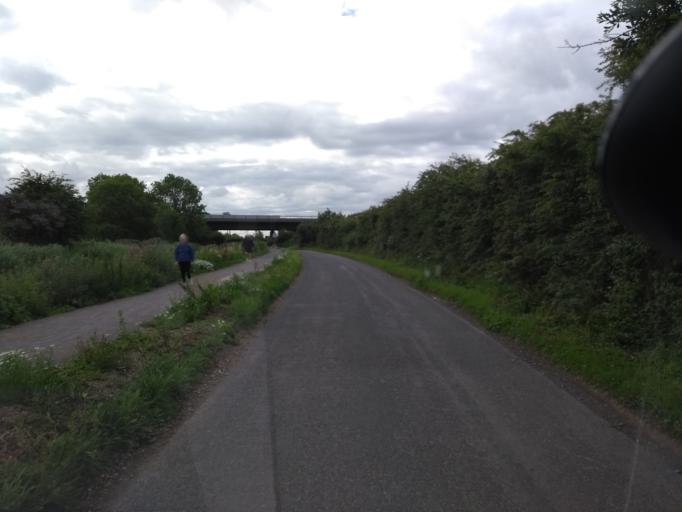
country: GB
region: England
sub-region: Somerset
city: Bridgwater
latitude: 51.1111
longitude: -2.9867
